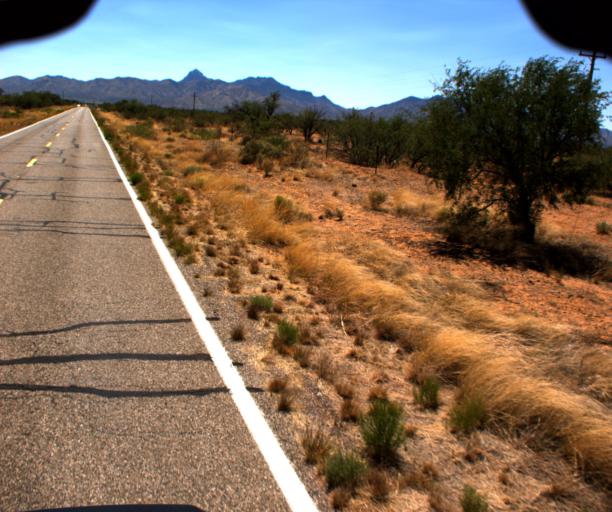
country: US
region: Arizona
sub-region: Pima County
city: Three Points
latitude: 31.8314
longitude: -111.4190
